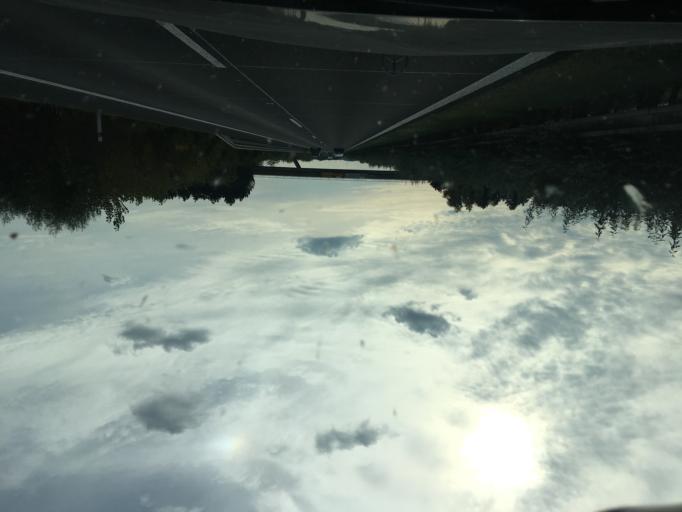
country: CZ
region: Central Bohemia
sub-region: Okres Nymburk
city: Sadska
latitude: 50.1196
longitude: 14.9900
